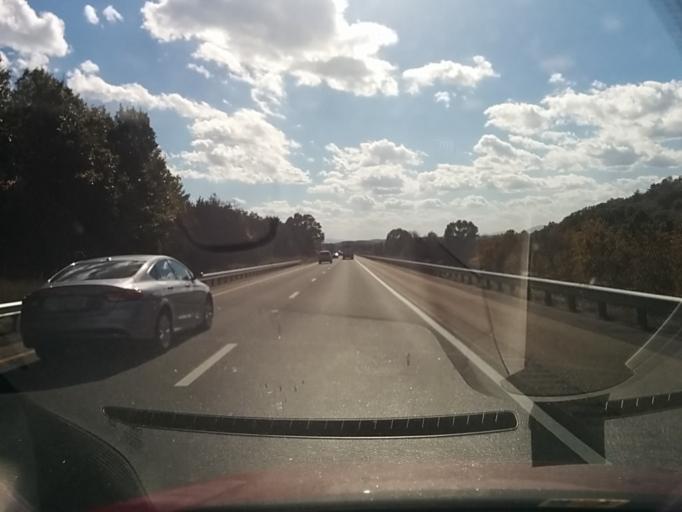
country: US
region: Virginia
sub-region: Rockbridge County
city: East Lexington
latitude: 37.8185
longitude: -79.3819
